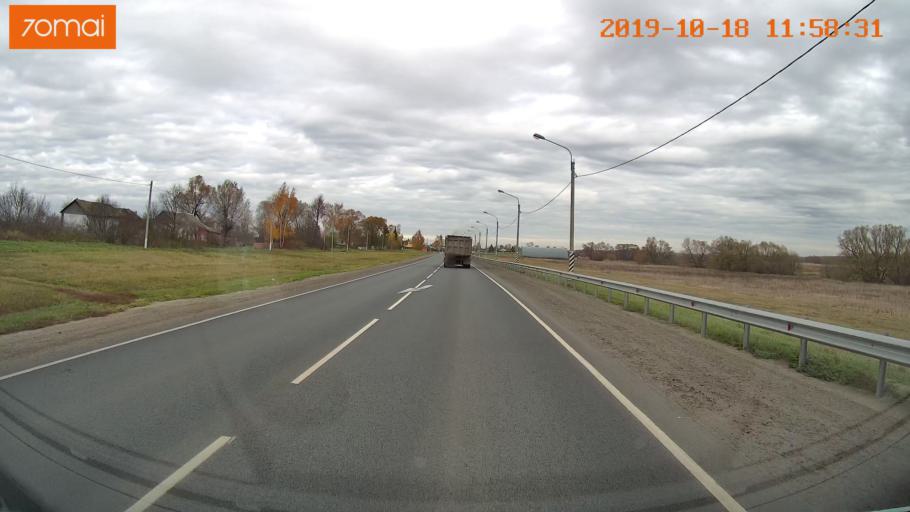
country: RU
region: Rjazan
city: Zakharovo
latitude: 54.2727
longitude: 39.1681
